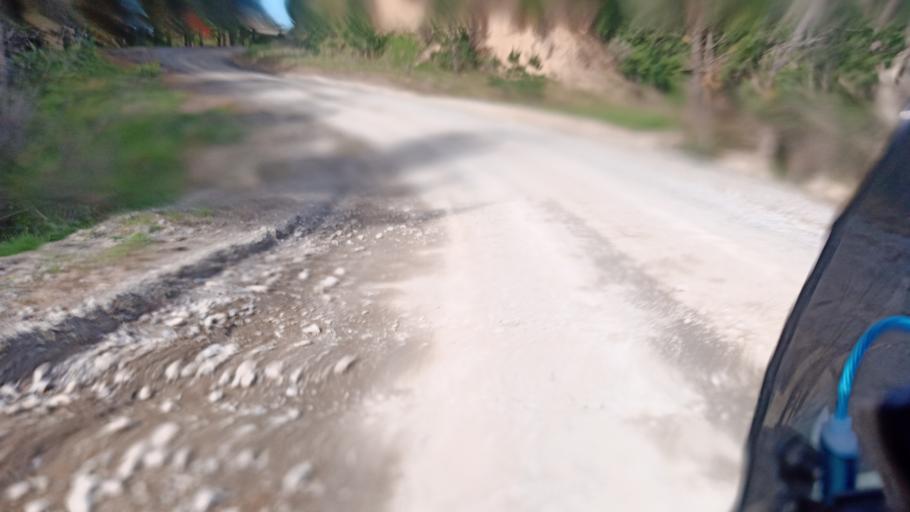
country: NZ
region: Gisborne
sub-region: Gisborne District
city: Gisborne
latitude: -38.1271
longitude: 178.1649
